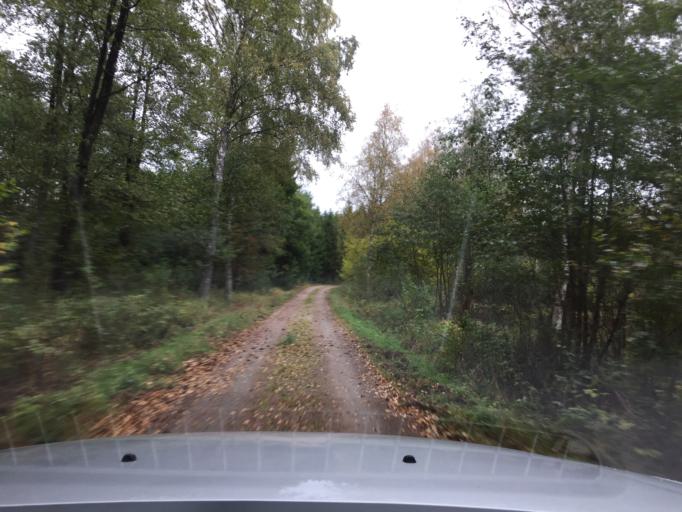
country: SE
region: Skane
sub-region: Hassleholms Kommun
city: Tormestorp
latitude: 56.0540
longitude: 13.7478
